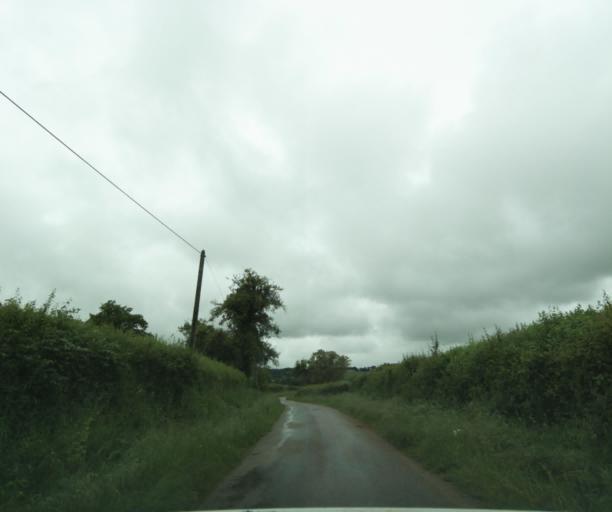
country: FR
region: Bourgogne
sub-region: Departement de Saone-et-Loire
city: Charolles
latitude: 46.4587
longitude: 4.3186
